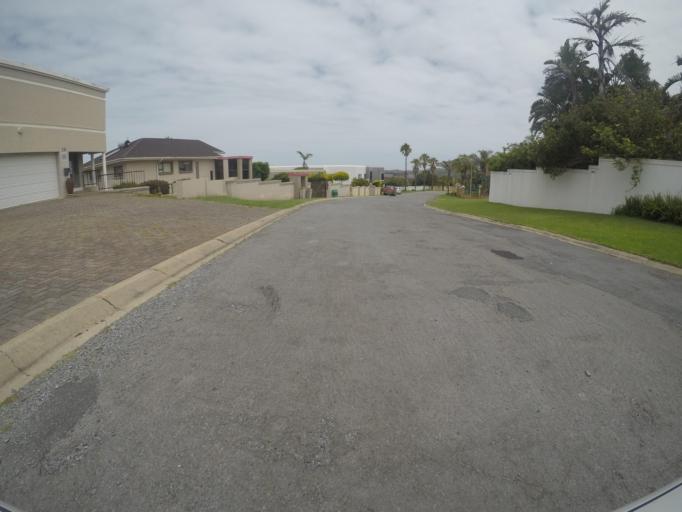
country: ZA
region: Eastern Cape
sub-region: Buffalo City Metropolitan Municipality
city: East London
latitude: -32.9798
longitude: 27.9518
